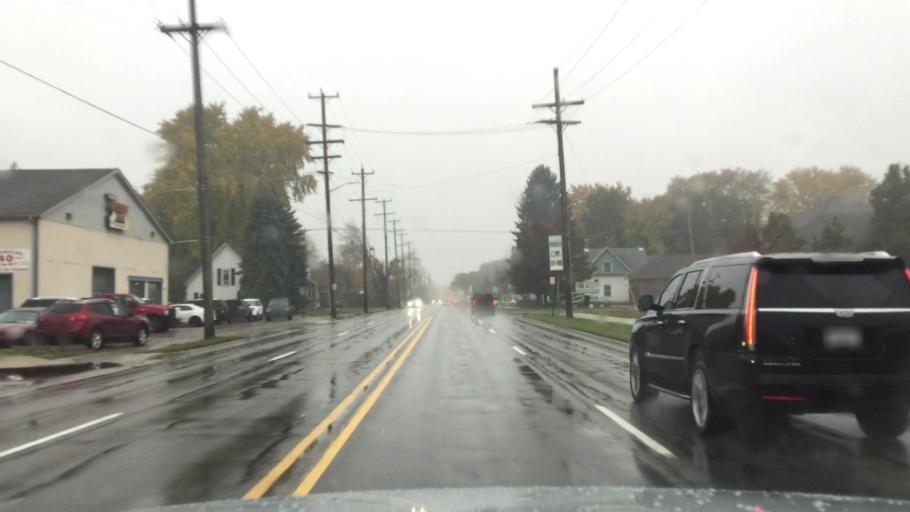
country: US
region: Michigan
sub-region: Macomb County
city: New Baltimore
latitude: 42.6844
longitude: -82.7320
